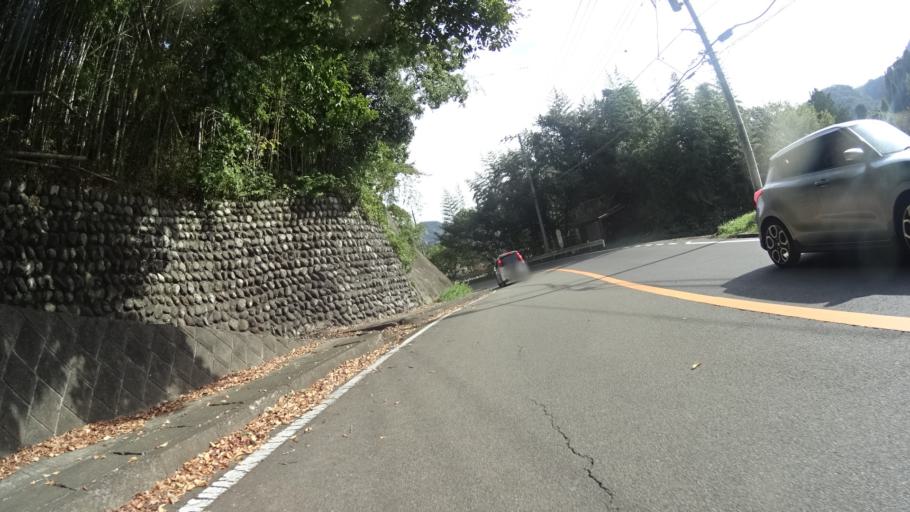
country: JP
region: Yamanashi
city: Uenohara
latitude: 35.5837
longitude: 139.1428
